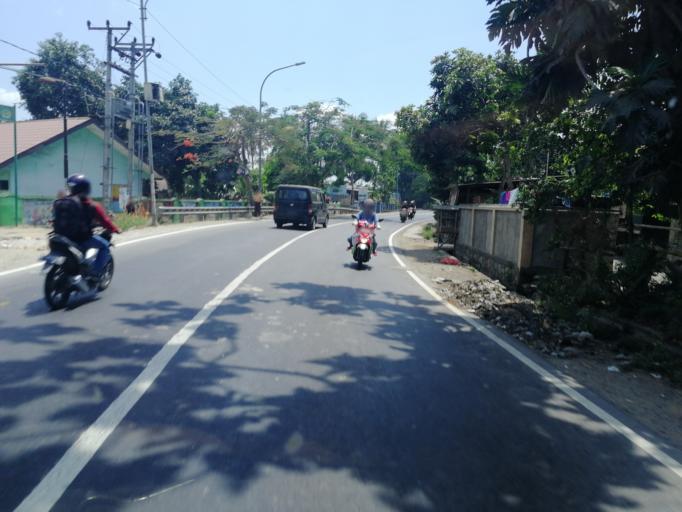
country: ID
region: West Nusa Tenggara
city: Jelateng Timur
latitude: -8.7079
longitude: 116.0790
